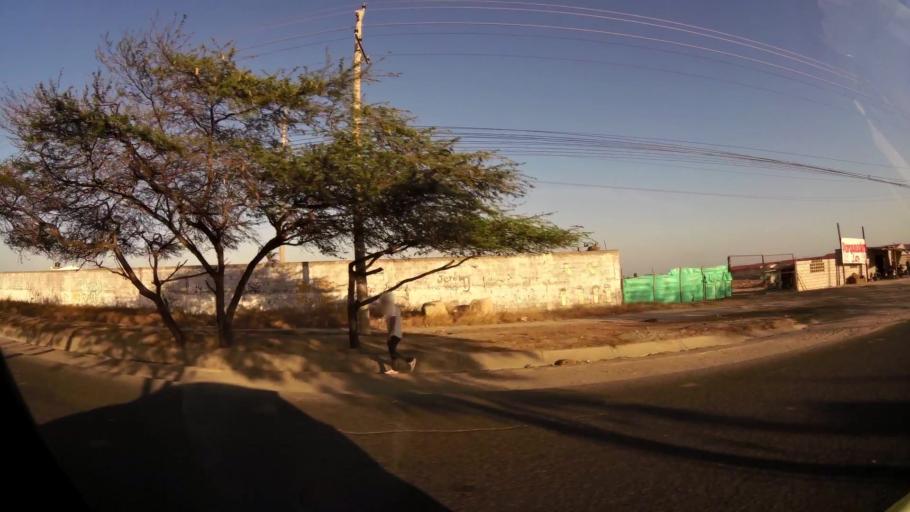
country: CO
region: Atlantico
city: Soledad
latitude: 10.9002
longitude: -74.8026
